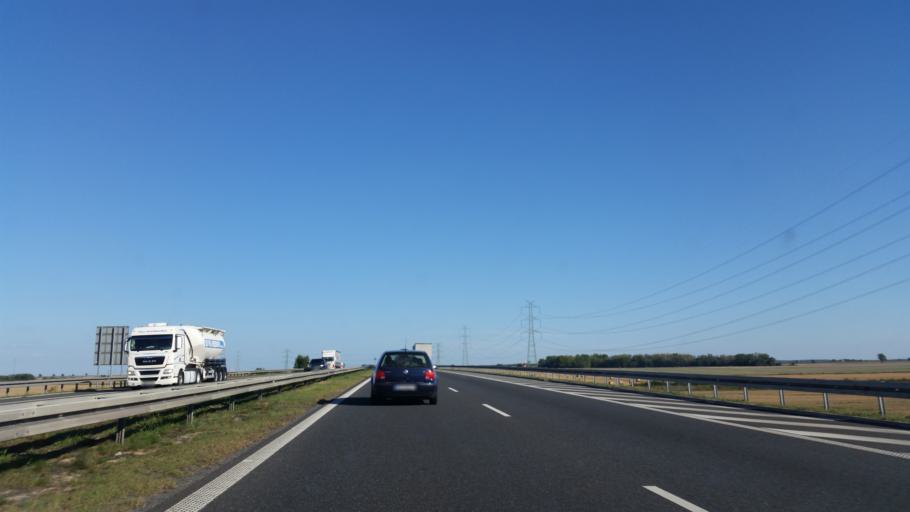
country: PL
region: Opole Voivodeship
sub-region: Powiat brzeski
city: Olszanka
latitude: 50.7500
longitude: 17.4430
